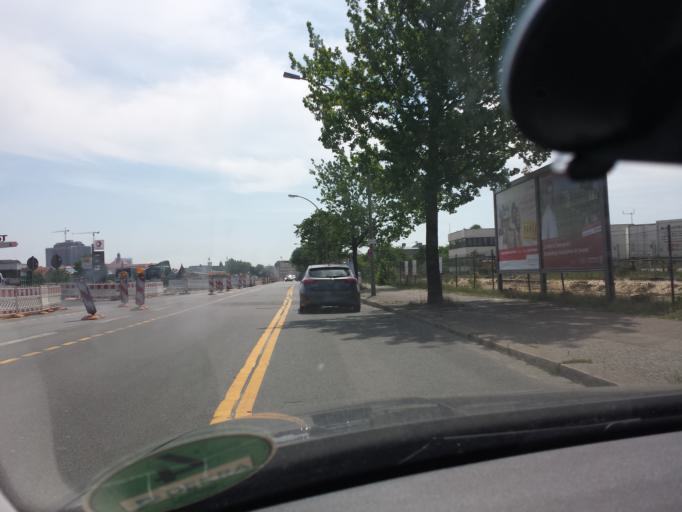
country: DE
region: Berlin
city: Wedding Bezirk
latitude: 52.5345
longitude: 13.3642
